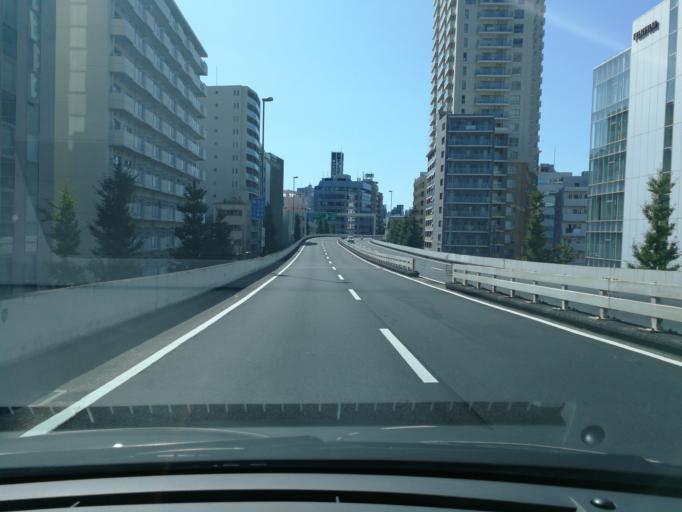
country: JP
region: Tokyo
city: Tokyo
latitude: 35.6272
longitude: 139.7194
